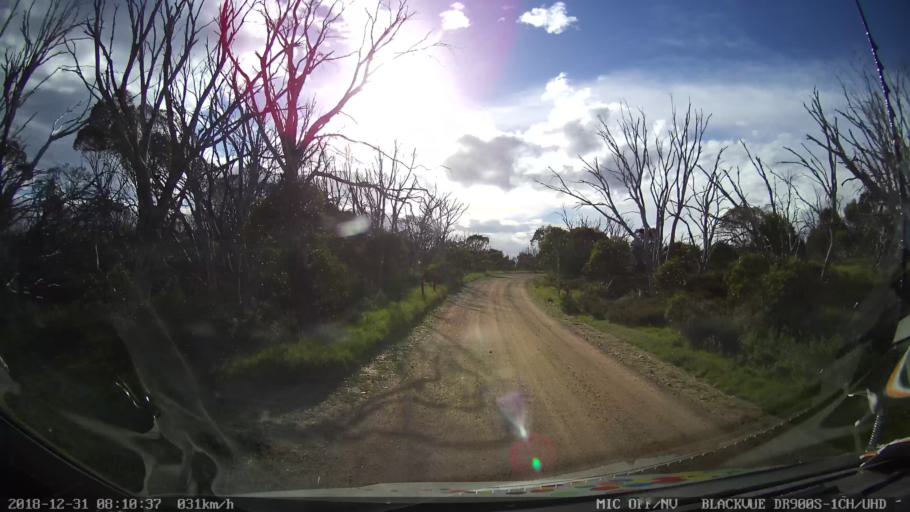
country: AU
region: New South Wales
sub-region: Snowy River
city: Jindabyne
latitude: -36.3834
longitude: 148.4221
